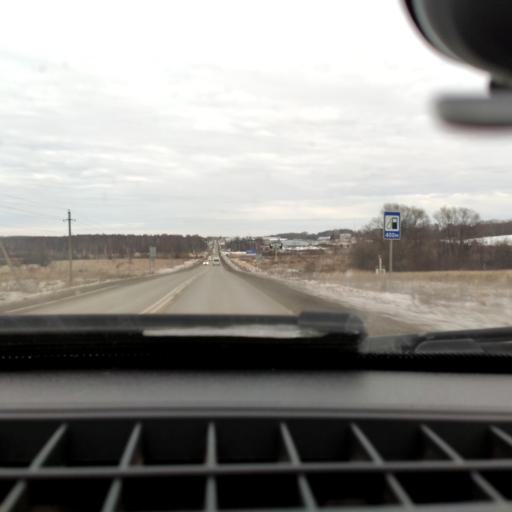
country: RU
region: Bashkortostan
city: Iglino
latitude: 54.8127
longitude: 56.3566
